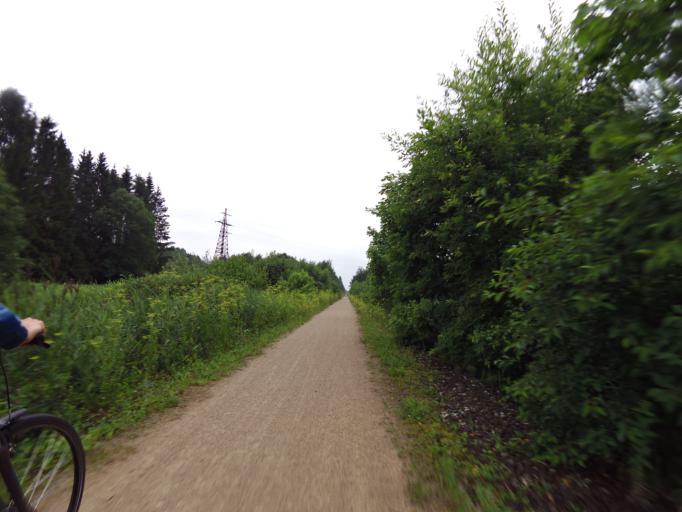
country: EE
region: Laeaene
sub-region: Lihula vald
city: Lihula
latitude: 58.9708
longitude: 23.8946
